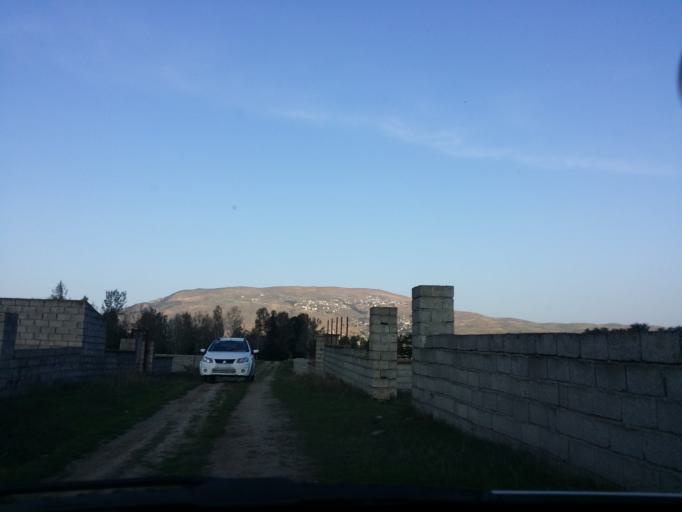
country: IR
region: Mazandaran
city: `Abbasabad
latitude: 36.5126
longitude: 51.1783
